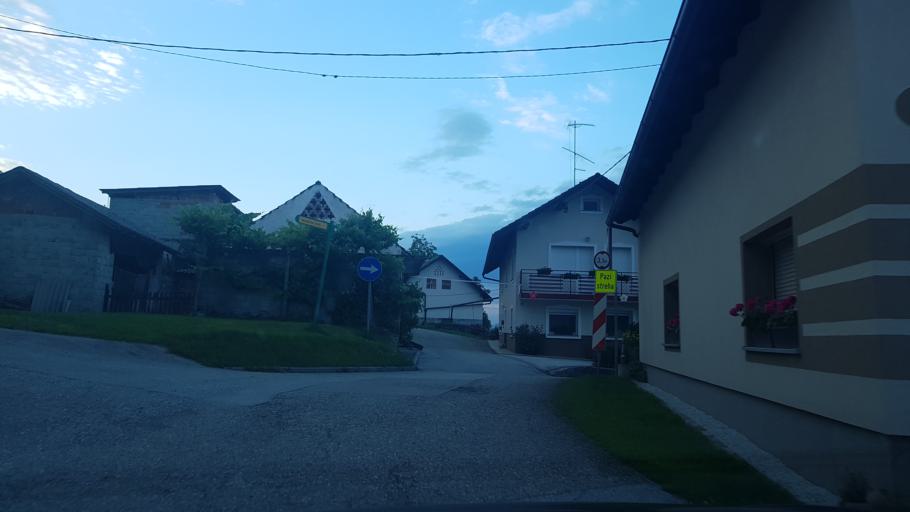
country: SI
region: Grosuplje
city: Smarje-Sap
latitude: 45.9205
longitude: 14.5888
